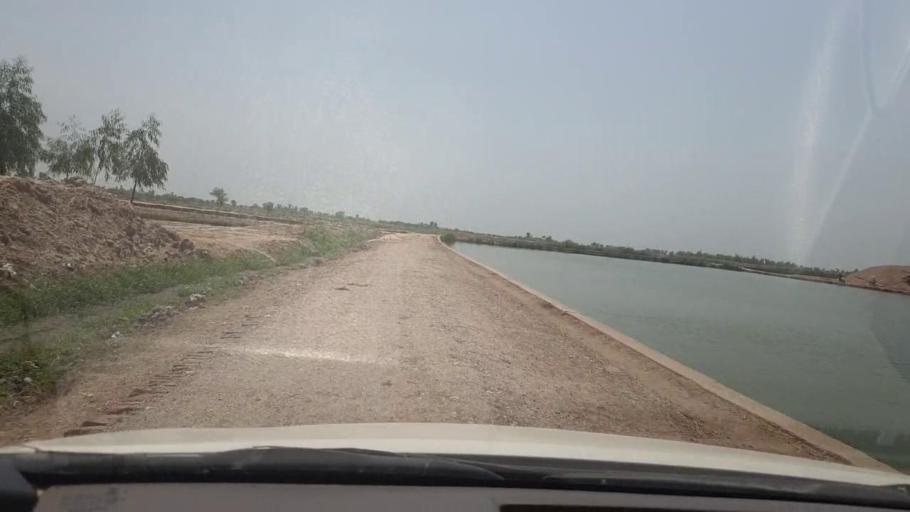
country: PK
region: Sindh
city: Garhi Yasin
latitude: 27.9072
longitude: 68.5534
